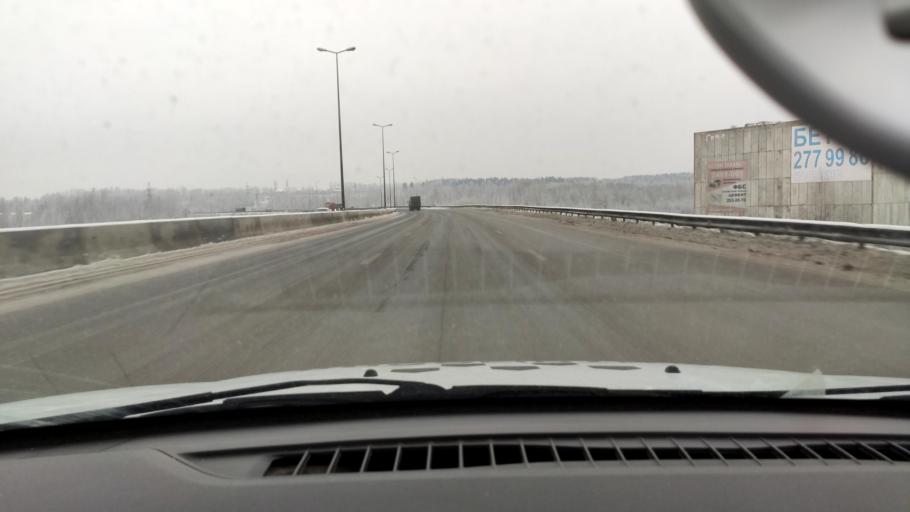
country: RU
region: Perm
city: Kondratovo
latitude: 58.0302
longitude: 56.0575
